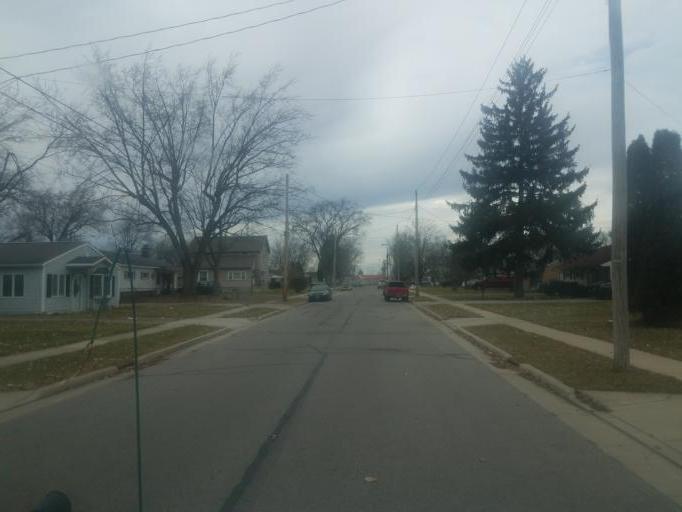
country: US
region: Ohio
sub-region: Marion County
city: Marion
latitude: 40.5941
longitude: -83.0994
